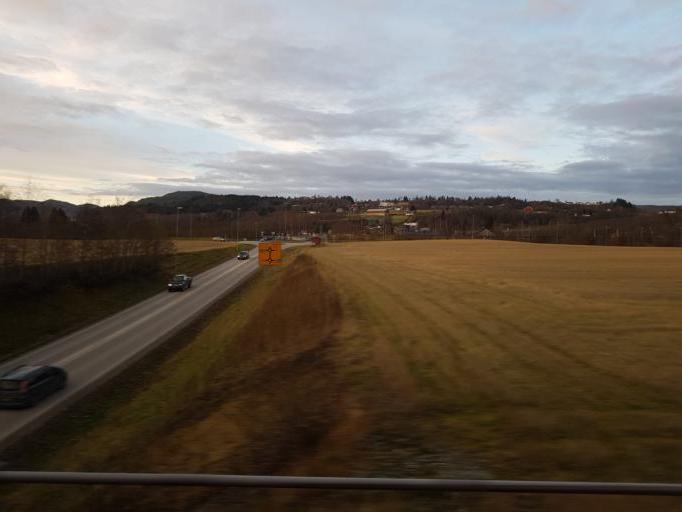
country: NO
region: Sor-Trondelag
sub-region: Melhus
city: Melhus
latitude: 63.2857
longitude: 10.2779
